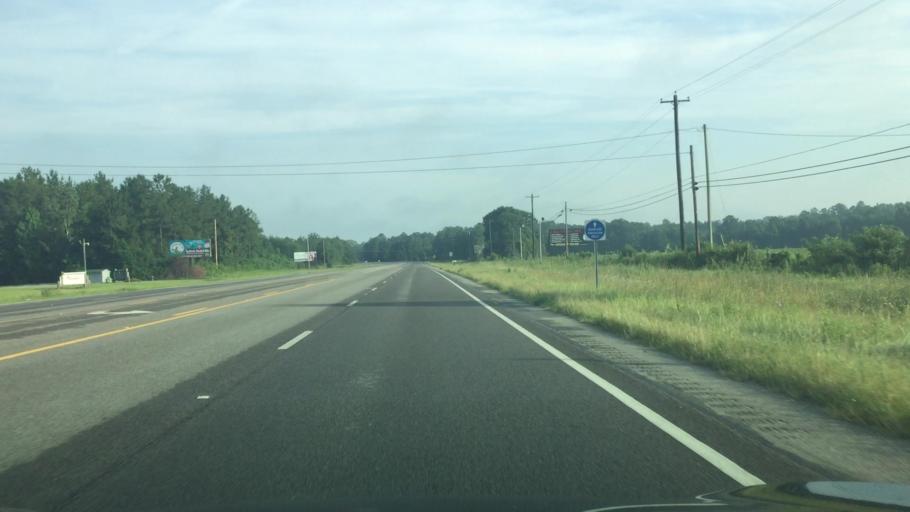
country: US
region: Alabama
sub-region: Covington County
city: Andalusia
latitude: 31.3411
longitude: -86.5231
